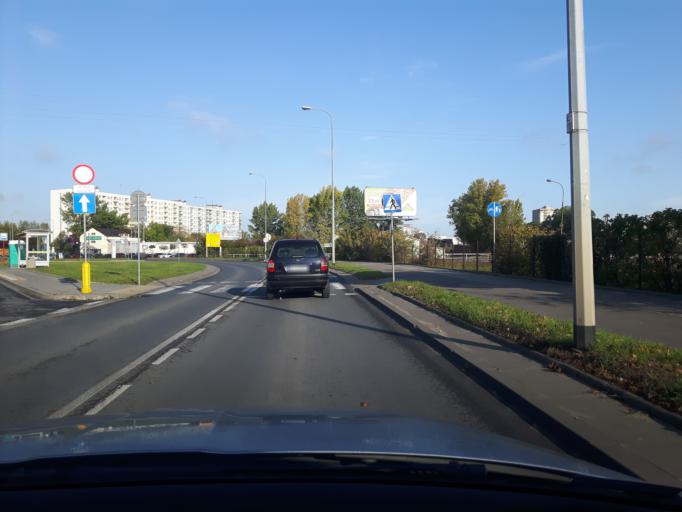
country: PL
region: Masovian Voivodeship
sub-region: Warszawa
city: Targowek
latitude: 52.2857
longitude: 21.0505
